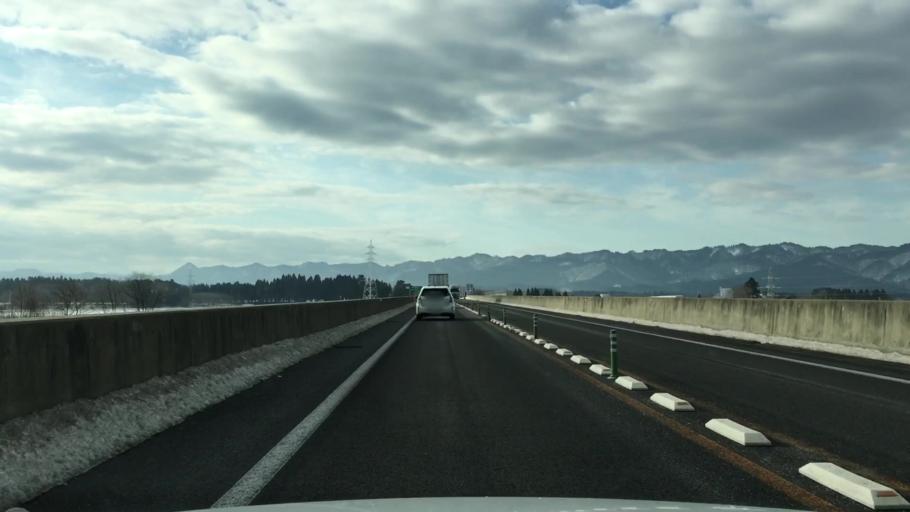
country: JP
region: Akita
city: Odate
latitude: 40.2658
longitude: 140.5265
